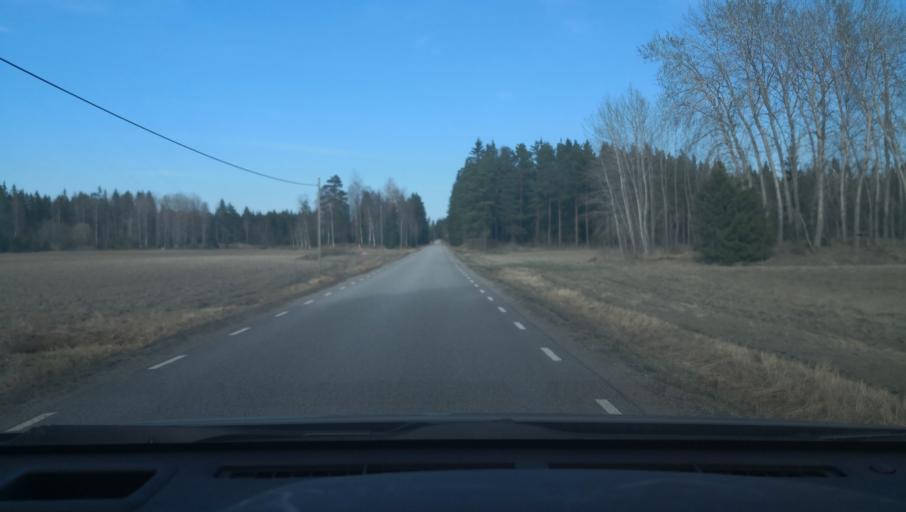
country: SE
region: Uppsala
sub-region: Heby Kommun
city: Heby
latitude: 59.9104
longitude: 16.8251
